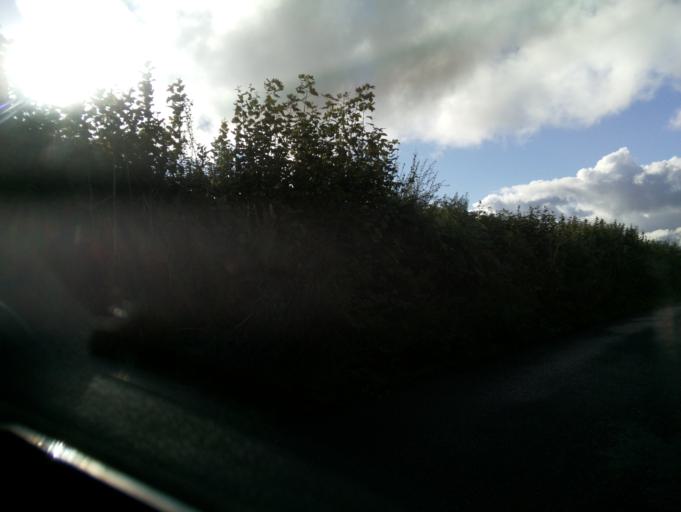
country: GB
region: England
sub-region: Devon
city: South Brent
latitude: 50.3964
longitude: -3.7790
